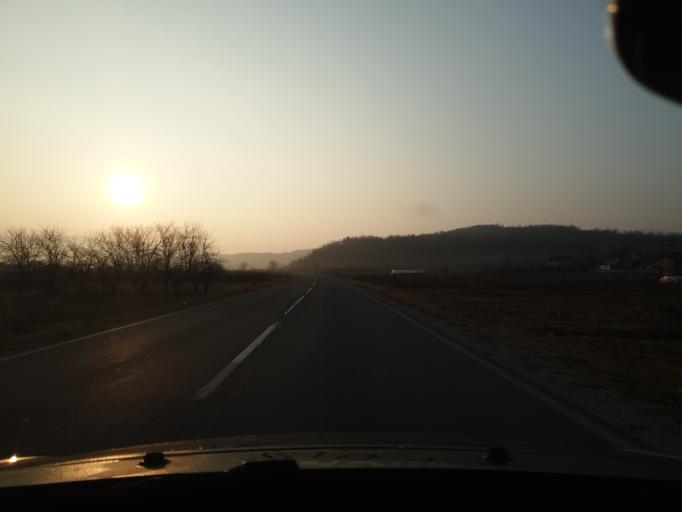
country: RS
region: Central Serbia
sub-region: Jablanicki Okrug
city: Leskovac
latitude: 42.9233
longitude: 22.0201
